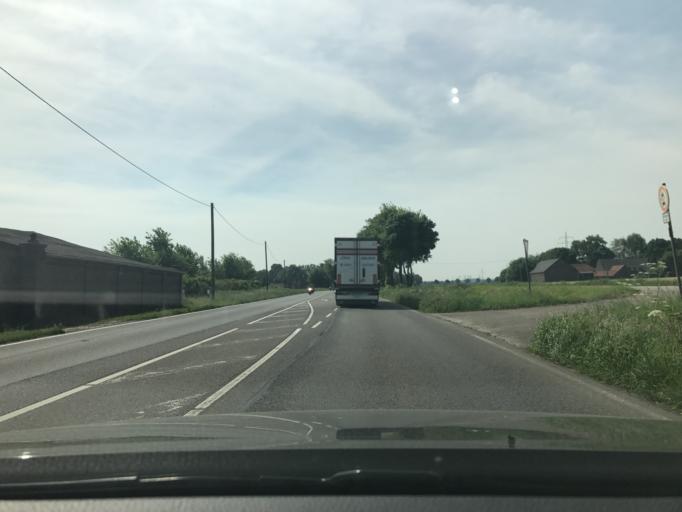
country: DE
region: North Rhine-Westphalia
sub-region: Regierungsbezirk Dusseldorf
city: Grefrath
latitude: 51.3477
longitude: 6.3239
